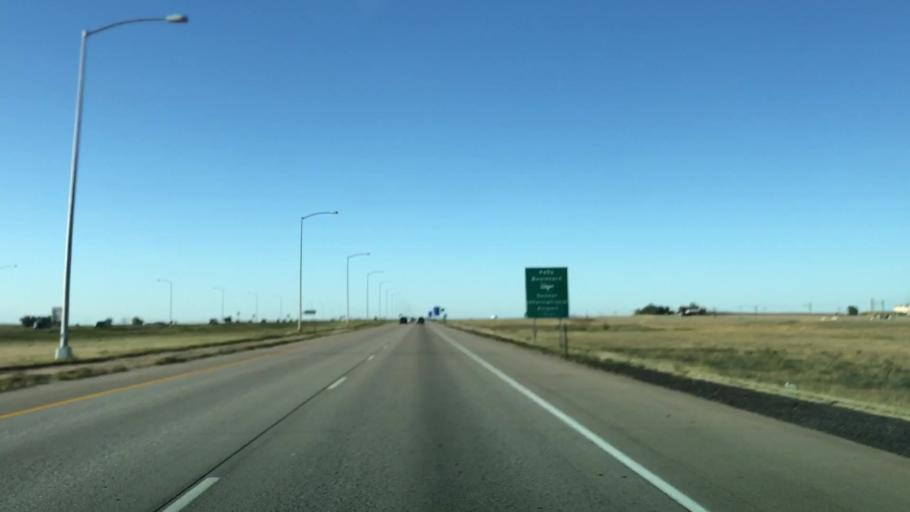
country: US
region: Colorado
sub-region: Adams County
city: Aurora
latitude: 39.8090
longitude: -104.7857
